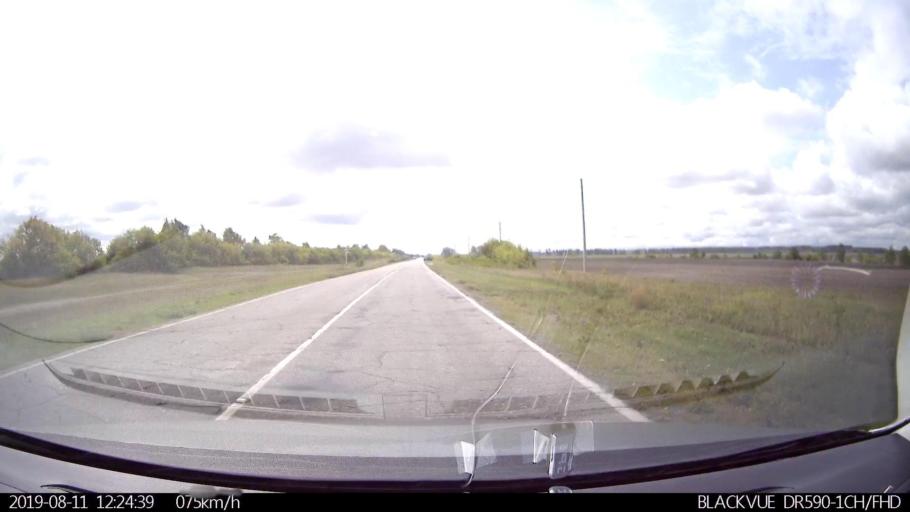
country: RU
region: Ulyanovsk
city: Ignatovka
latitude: 53.8812
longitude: 47.9470
